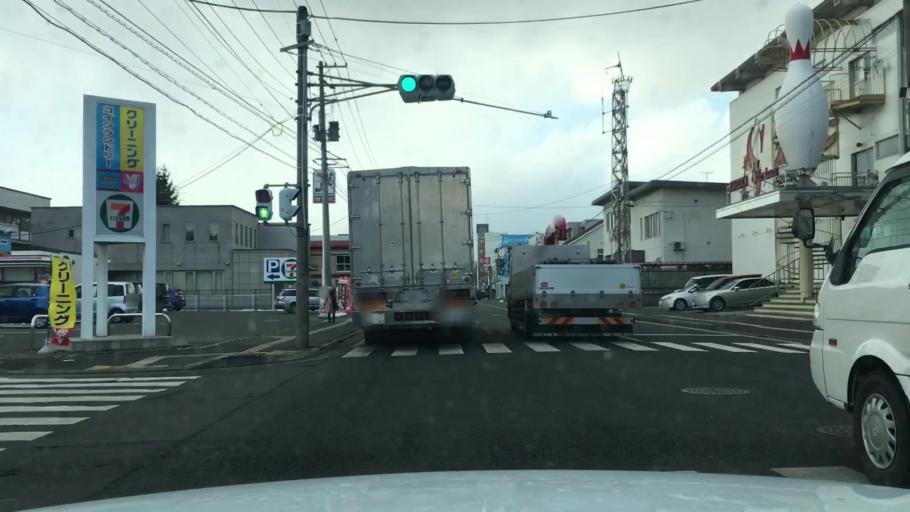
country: JP
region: Iwate
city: Morioka-shi
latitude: 39.6925
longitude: 141.1714
